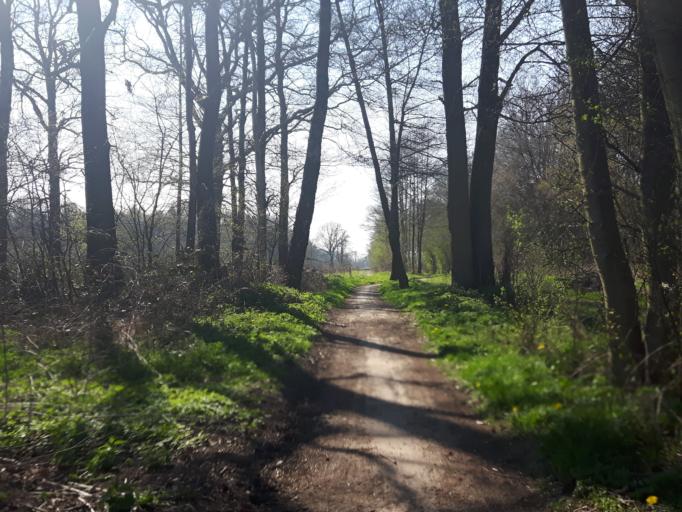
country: NL
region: Overijssel
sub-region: Gemeente Haaksbergen
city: Haaksbergen
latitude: 52.1577
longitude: 6.8171
